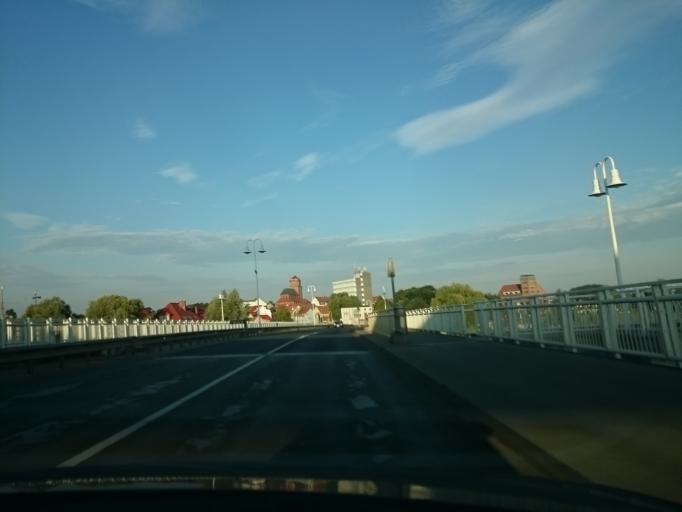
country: DE
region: Mecklenburg-Vorpommern
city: Wolgast
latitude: 54.0549
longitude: 13.7866
